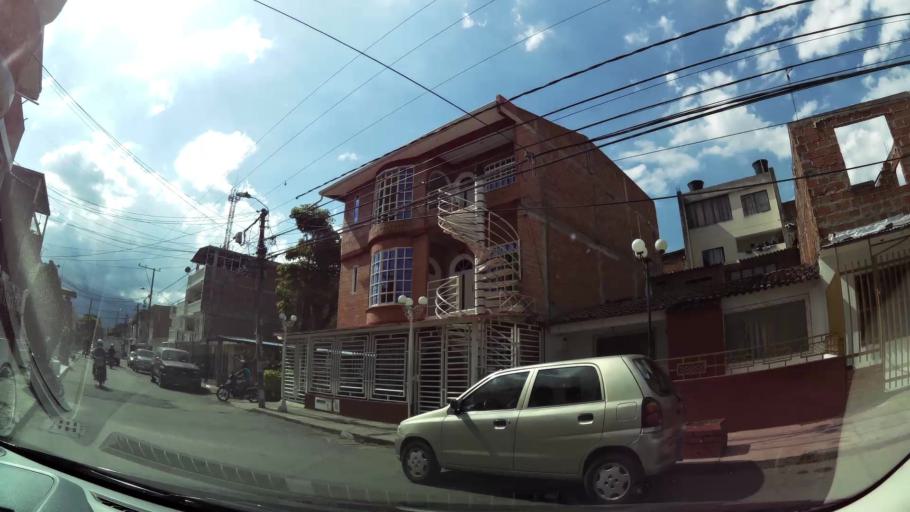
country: CO
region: Valle del Cauca
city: Cali
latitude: 3.4191
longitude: -76.5135
